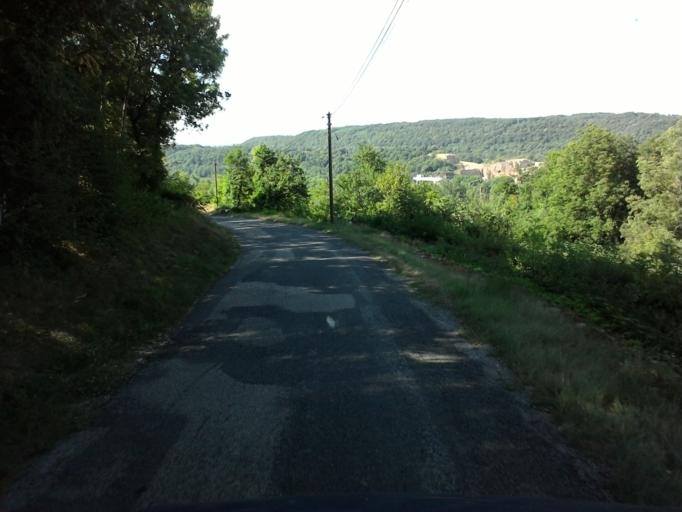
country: FR
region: Rhone-Alpes
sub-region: Departement de l'Ain
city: Sault-Brenaz
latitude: 45.8594
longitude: 5.4087
